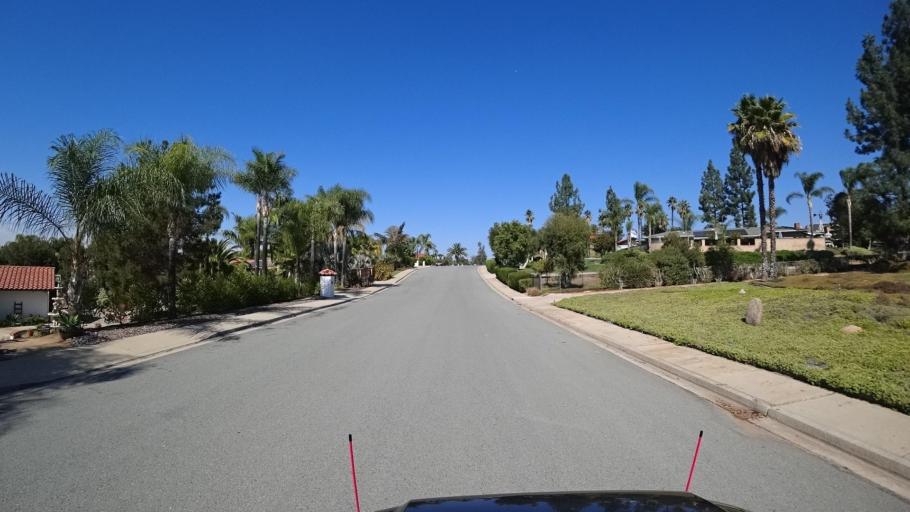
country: US
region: California
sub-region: San Diego County
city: Granite Hills
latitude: 32.7846
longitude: -116.9008
